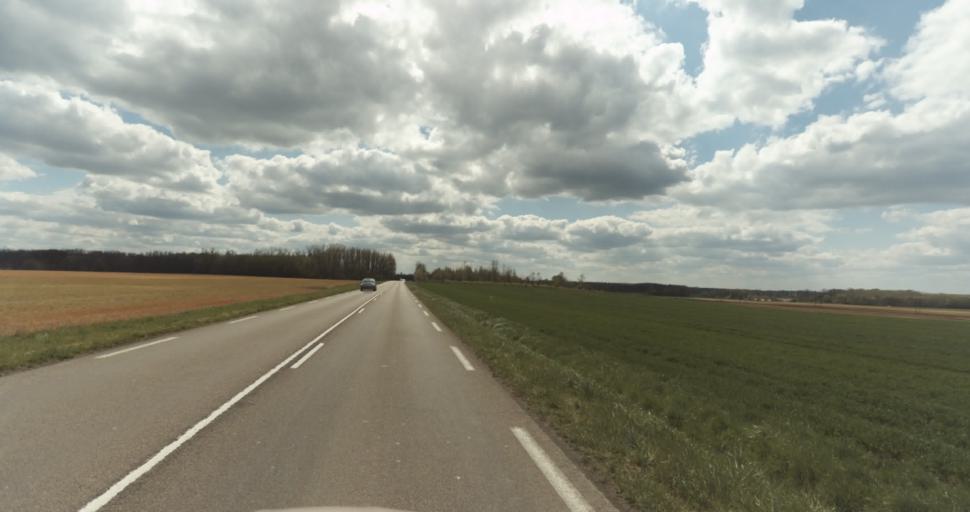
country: FR
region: Bourgogne
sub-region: Departement de la Cote-d'Or
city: Auxonne
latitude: 47.1726
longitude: 5.4022
